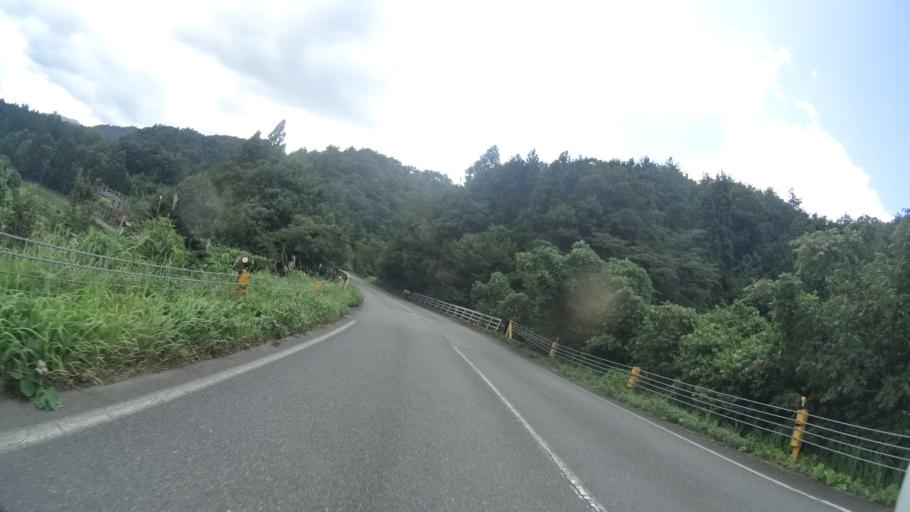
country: JP
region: Yamaguchi
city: Hagi
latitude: 34.5519
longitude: 131.5989
